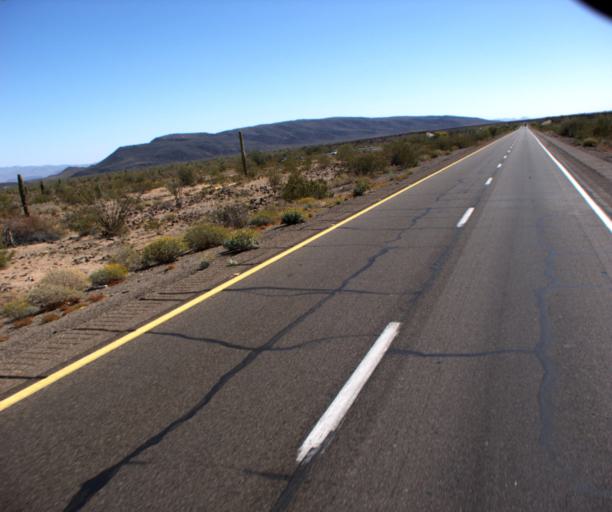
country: US
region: Arizona
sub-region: La Paz County
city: Quartzsite
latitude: 33.6567
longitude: -113.9716
